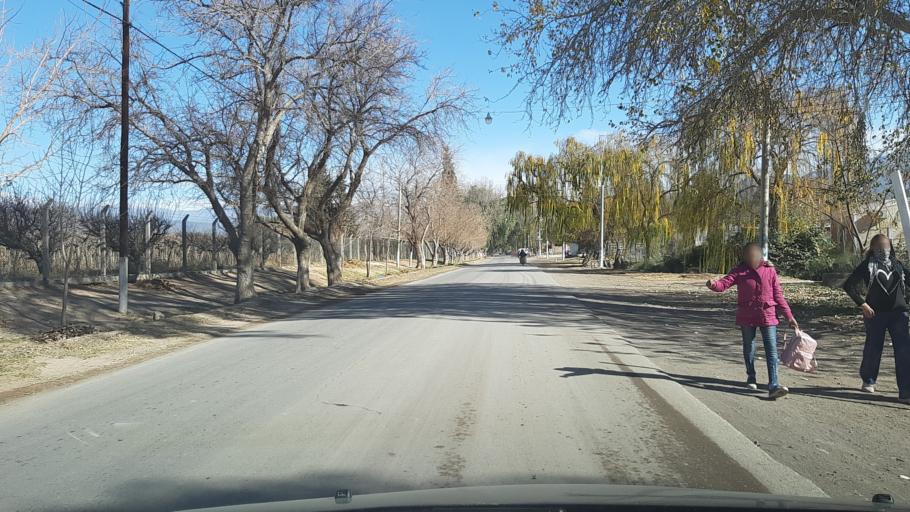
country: AR
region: San Juan
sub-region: Departamento de Zonda
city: Zonda
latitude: -31.4610
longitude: -68.7308
